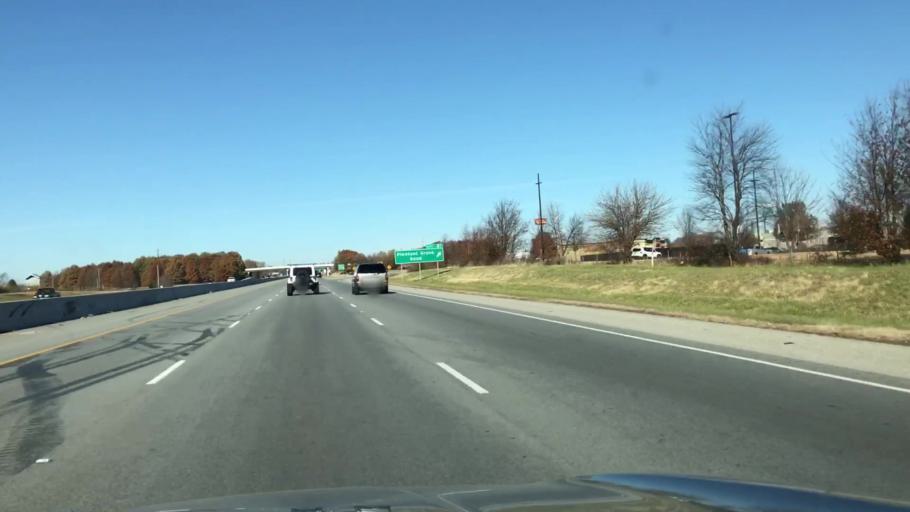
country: US
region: Arkansas
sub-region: Benton County
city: Lowell
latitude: 36.2789
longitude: -94.1530
